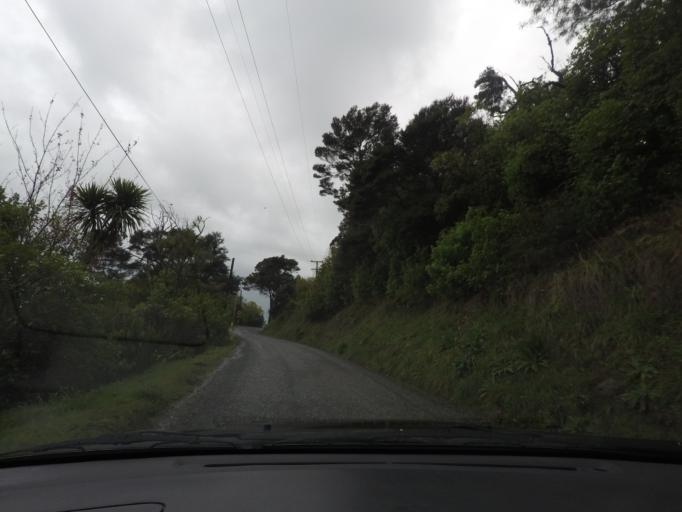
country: NZ
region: Auckland
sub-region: Auckland
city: Warkworth
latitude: -36.4835
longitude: 174.7277
